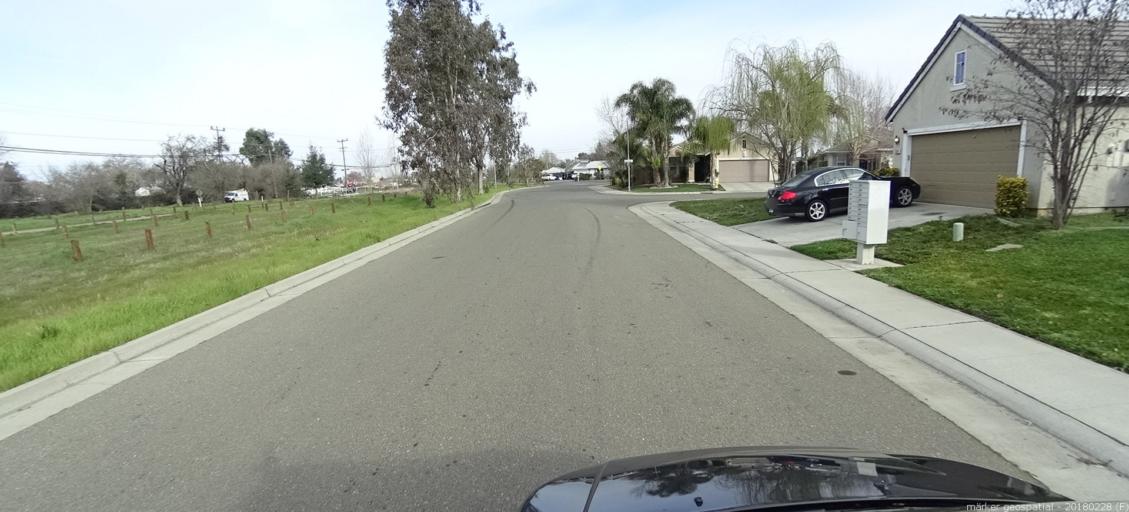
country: US
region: California
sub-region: Sacramento County
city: Elverta
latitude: 38.7041
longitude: -121.4566
